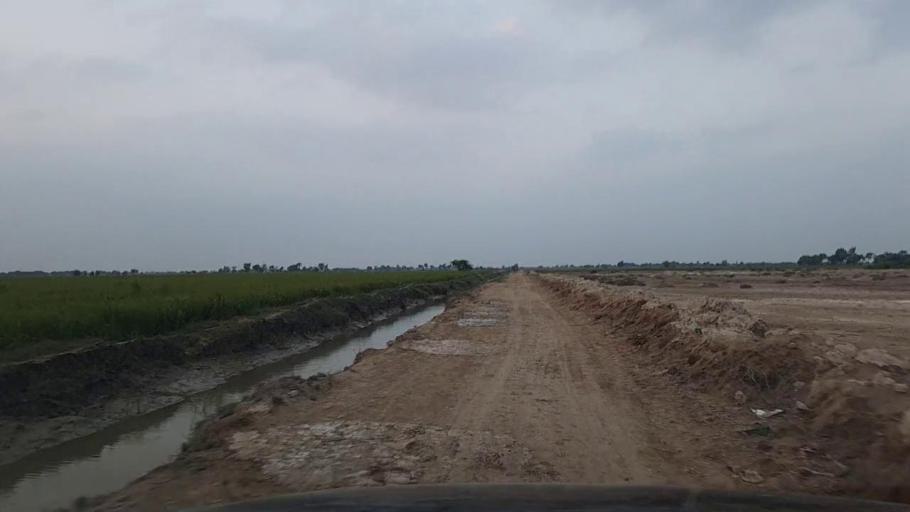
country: PK
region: Sindh
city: Jati
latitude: 24.5015
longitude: 68.3931
